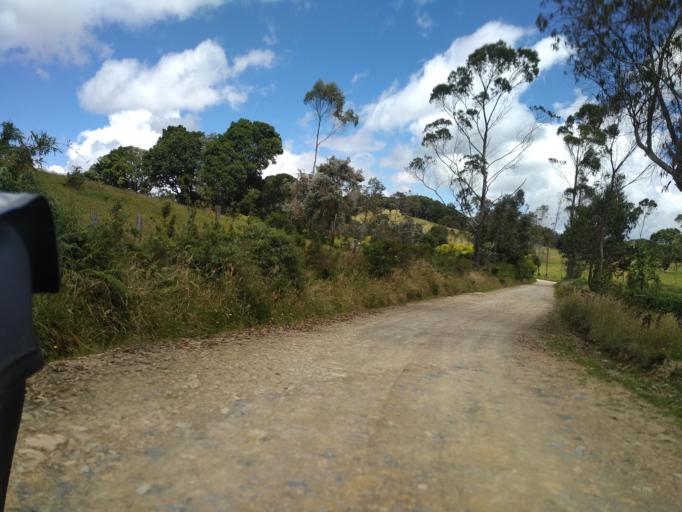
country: CO
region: Boyaca
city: Duitama
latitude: 5.9387
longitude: -73.1164
